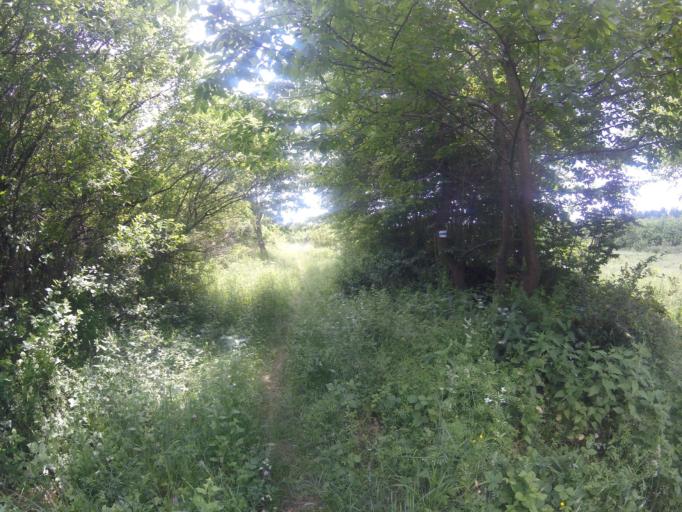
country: HU
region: Veszprem
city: Urkut
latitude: 47.0729
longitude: 17.6497
